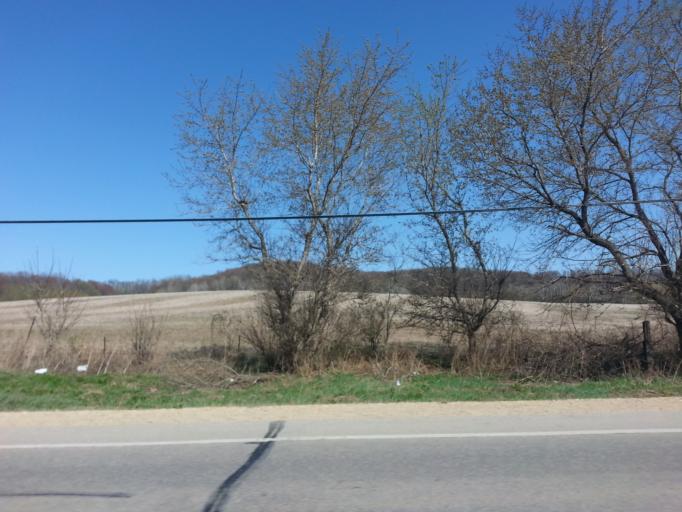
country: US
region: Wisconsin
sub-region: Dunn County
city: Menomonie
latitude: 44.8461
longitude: -91.9245
